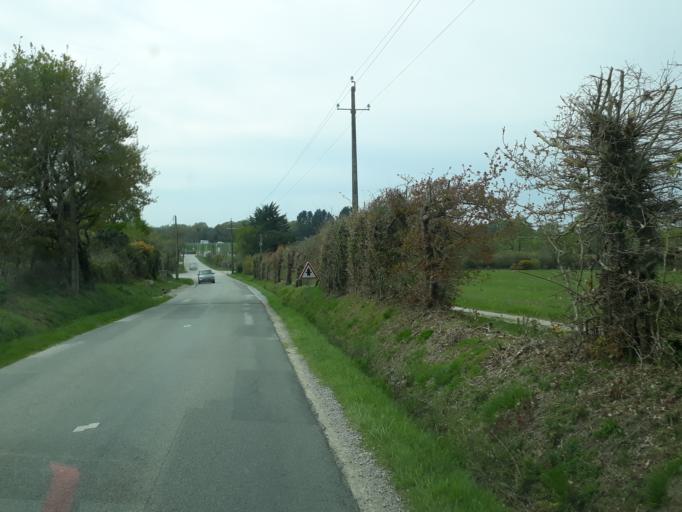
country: FR
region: Brittany
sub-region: Departement du Morbihan
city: Theix
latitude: 47.6362
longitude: -2.6460
